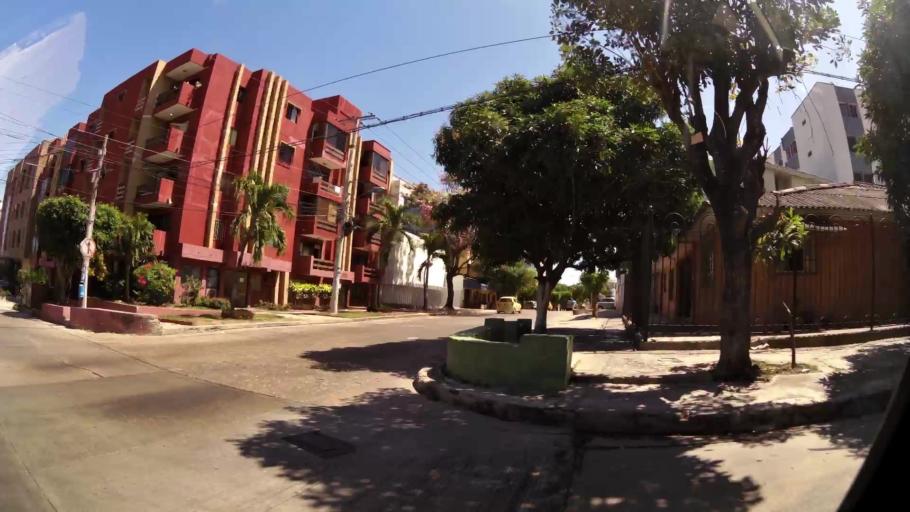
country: CO
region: Atlantico
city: Barranquilla
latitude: 10.9888
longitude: -74.8077
